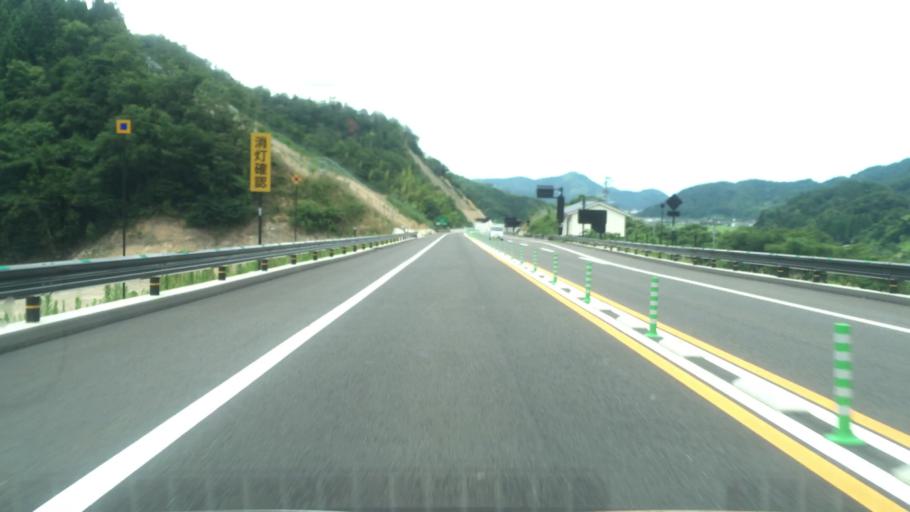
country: JP
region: Tottori
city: Tottori
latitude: 35.6233
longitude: 134.5115
